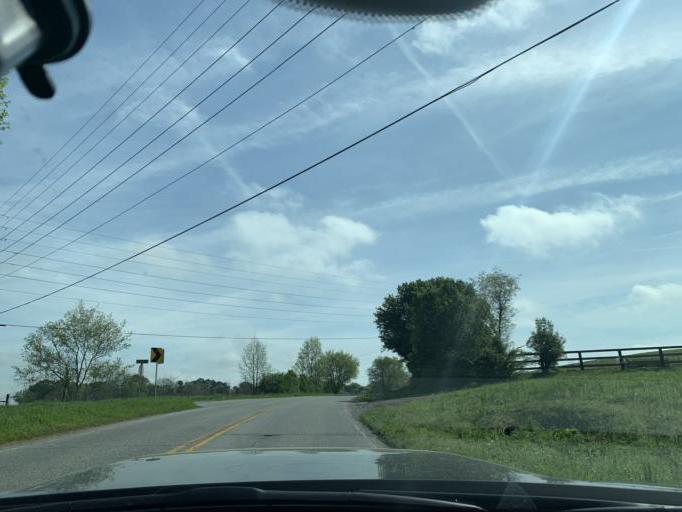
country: US
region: Georgia
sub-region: Forsyth County
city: Cumming
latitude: 34.2427
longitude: -84.0865
